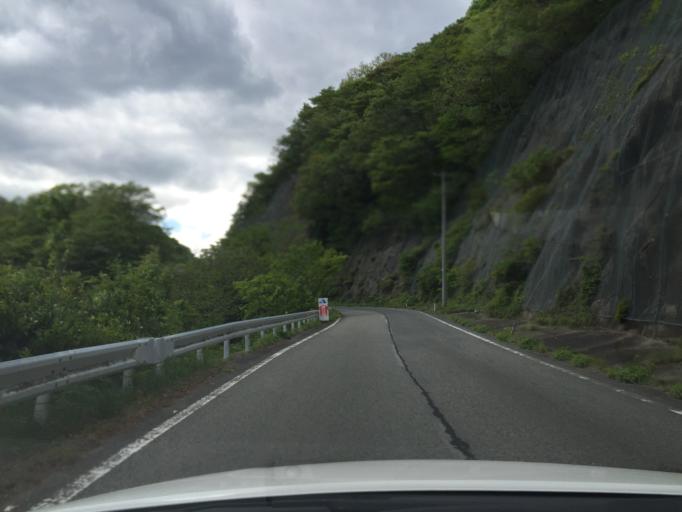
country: JP
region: Miyagi
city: Marumori
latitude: 37.7168
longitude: 140.8414
